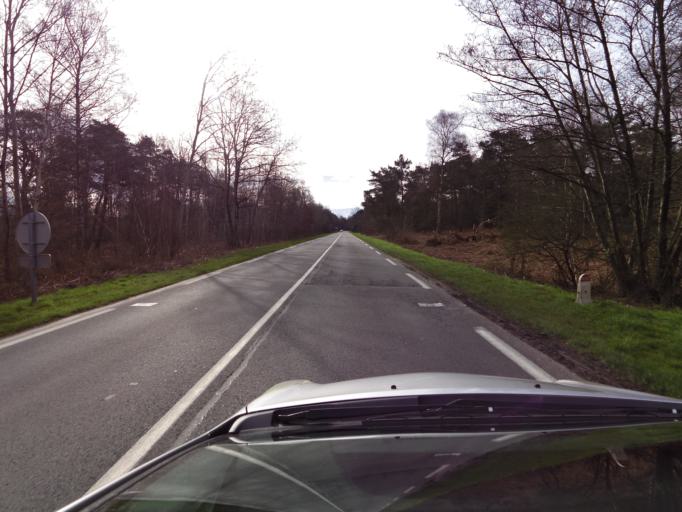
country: FR
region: Picardie
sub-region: Departement de l'Oise
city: Ver-sur-Launette
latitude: 49.1414
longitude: 2.6840
